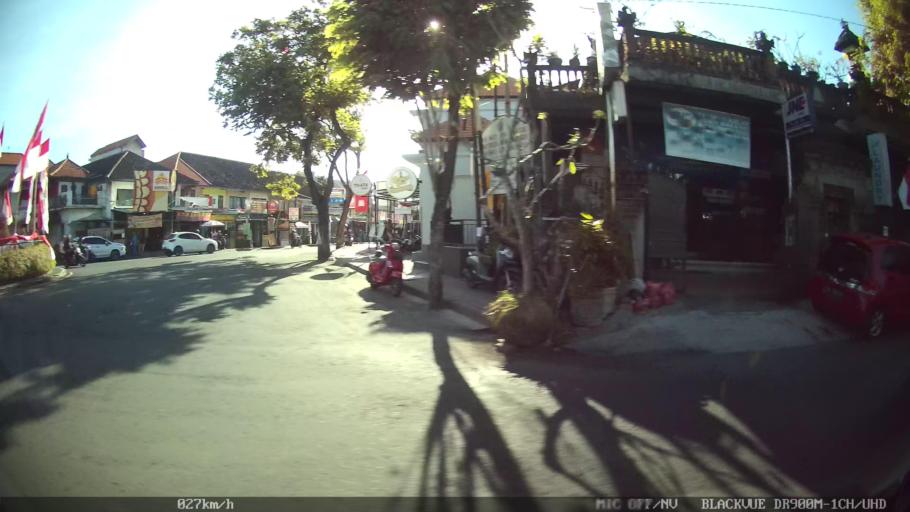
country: ID
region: Bali
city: Banjar Gunungpande
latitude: -8.6285
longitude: 115.1725
